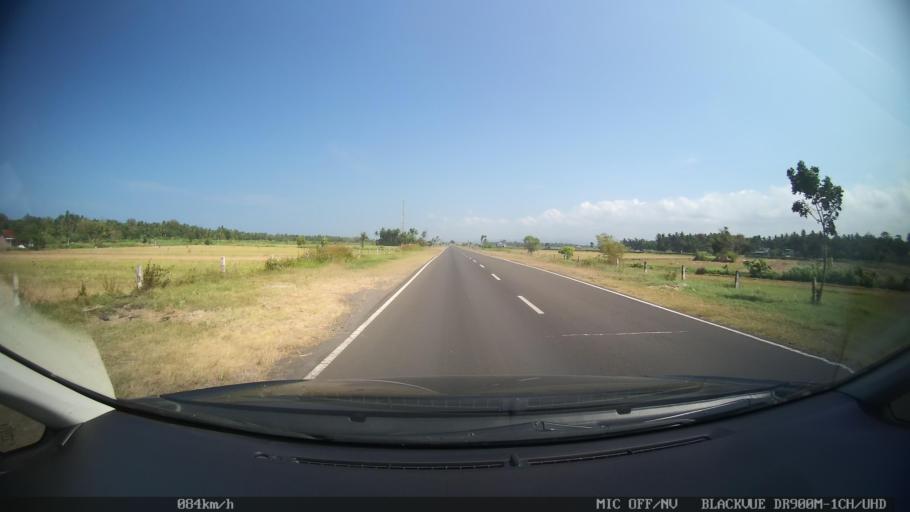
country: ID
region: Daerah Istimewa Yogyakarta
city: Srandakan
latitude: -7.9557
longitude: 110.1979
